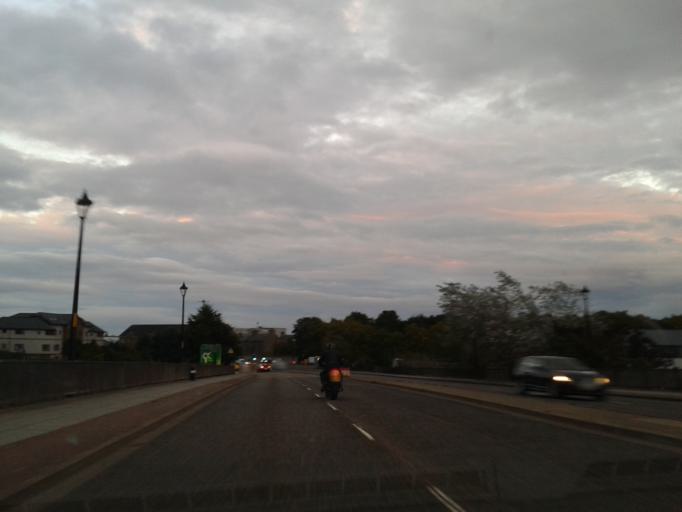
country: GB
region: Scotland
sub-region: Highland
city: Inverness
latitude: 57.4817
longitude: -4.2331
